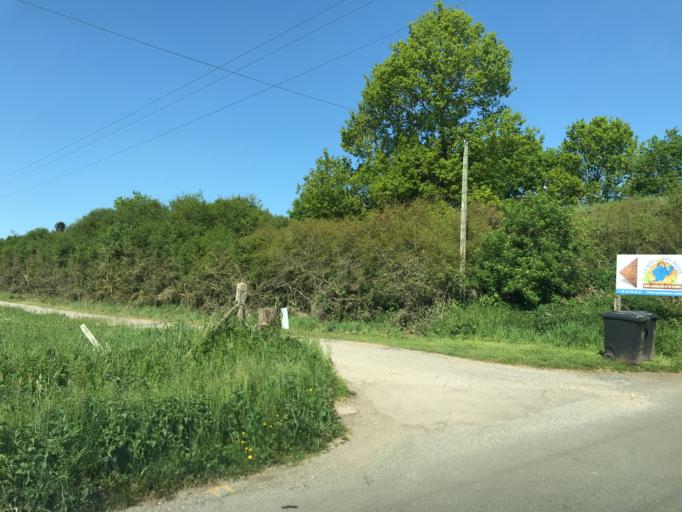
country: FR
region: Haute-Normandie
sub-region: Departement de l'Eure
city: Verneuil-sur-Avre
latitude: 48.7470
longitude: 0.9709
